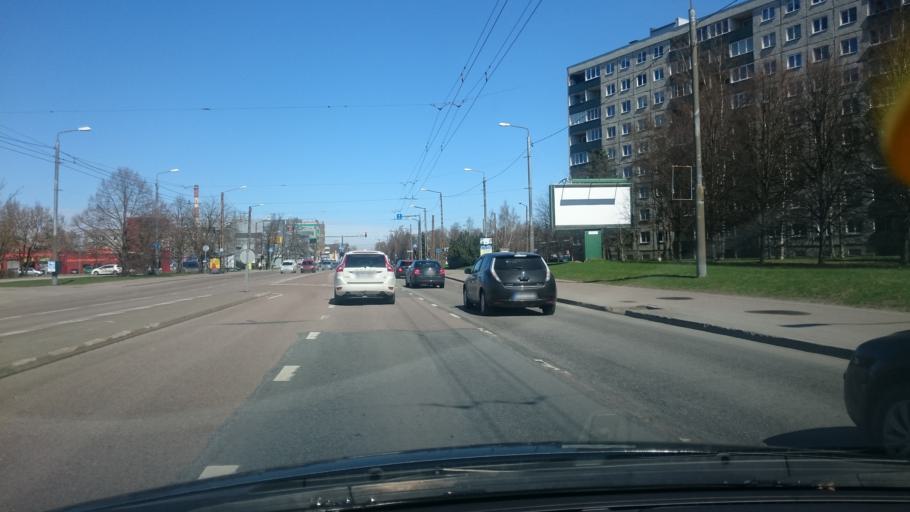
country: EE
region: Harju
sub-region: Tallinna linn
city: Tallinn
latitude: 59.4130
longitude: 24.6895
